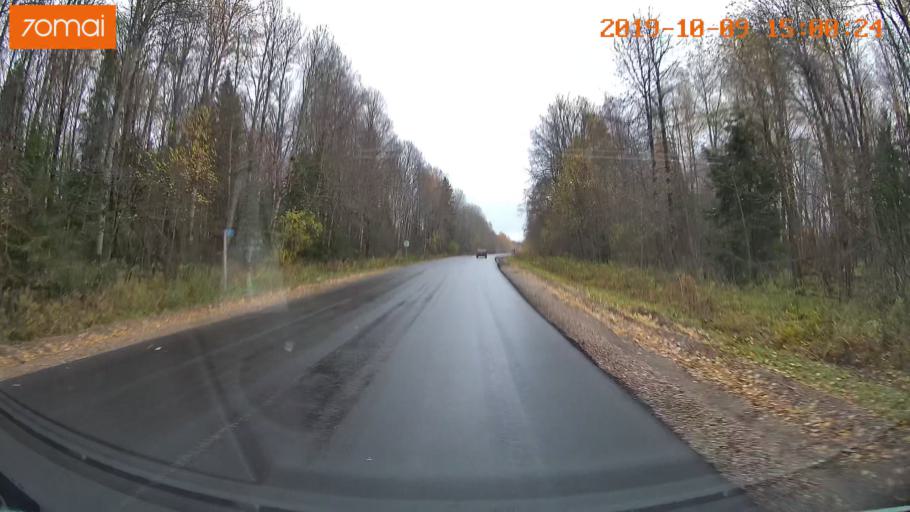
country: RU
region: Kostroma
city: Chistyye Bory
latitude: 58.3095
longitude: 41.6776
